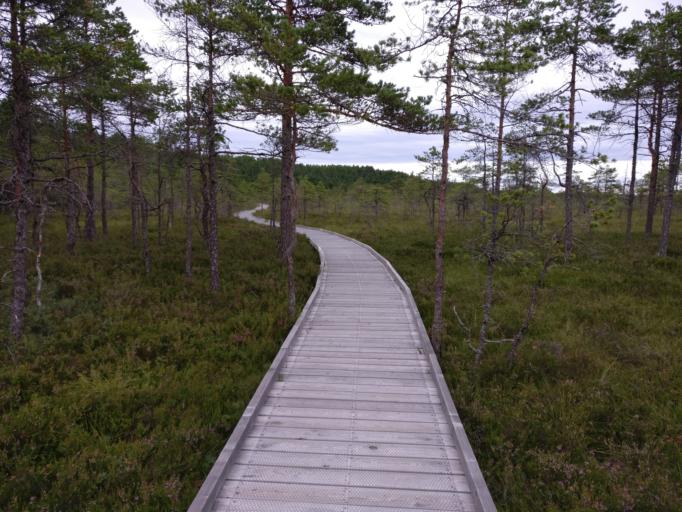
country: EE
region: Paernumaa
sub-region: Vaendra vald (alev)
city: Vandra
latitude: 58.4933
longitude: 24.9857
